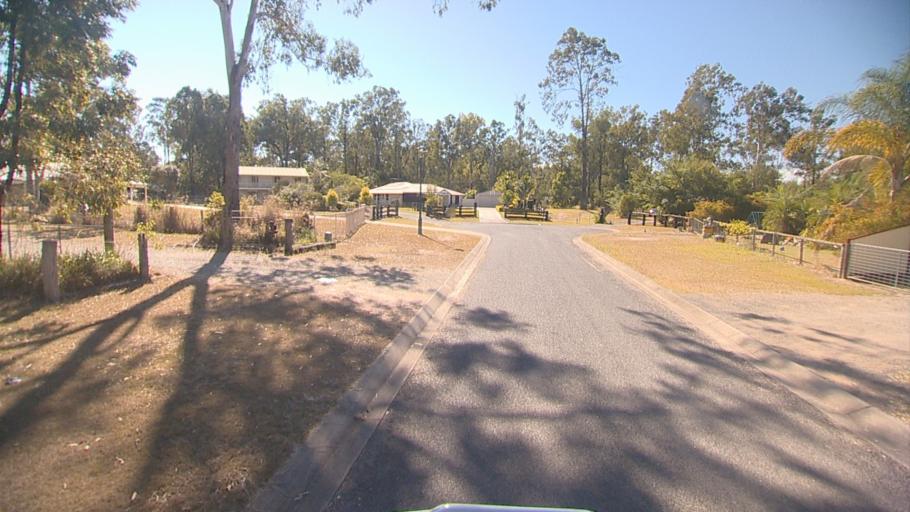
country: AU
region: Queensland
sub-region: Logan
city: North Maclean
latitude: -27.8162
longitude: 152.9468
